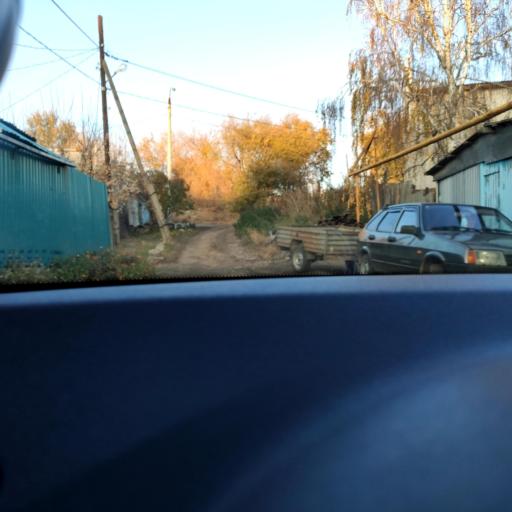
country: RU
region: Samara
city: Samara
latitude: 53.1936
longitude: 50.1549
